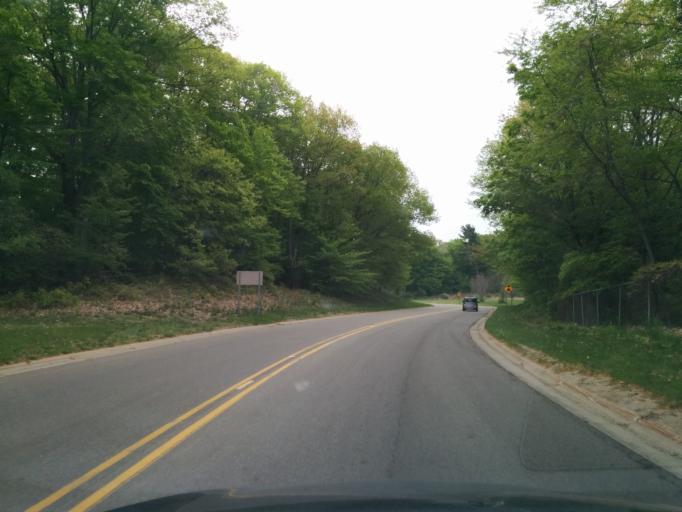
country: US
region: Michigan
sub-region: Ottawa County
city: Grand Haven
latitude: 43.0240
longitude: -86.2178
